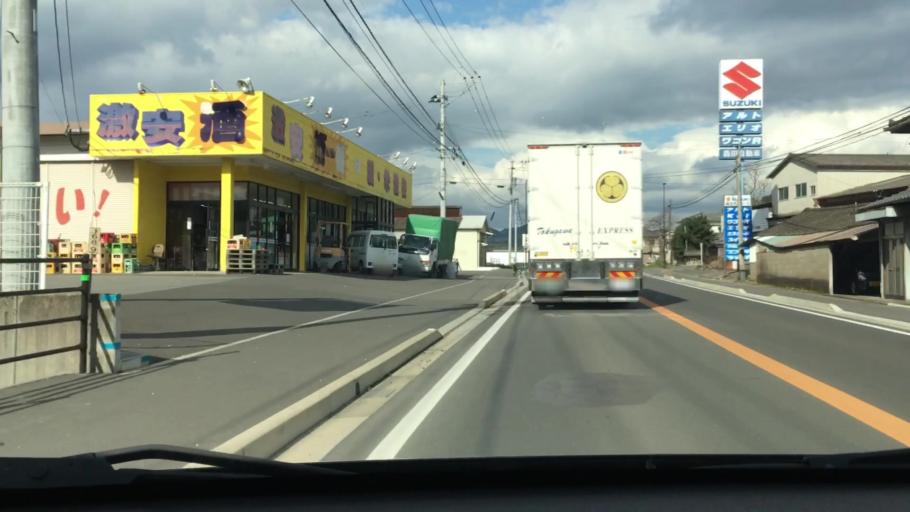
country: JP
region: Oita
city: Usuki
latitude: 33.0351
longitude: 131.6893
